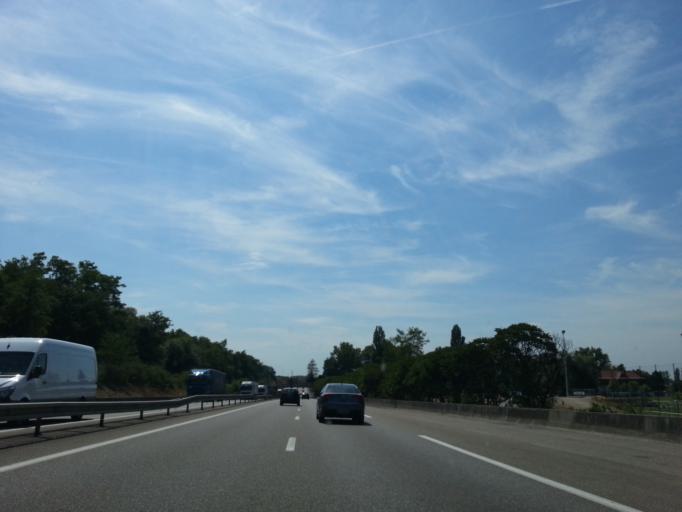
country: FR
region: Alsace
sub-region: Departement du Haut-Rhin
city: Horbourg-Wihr
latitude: 48.0837
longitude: 7.3839
